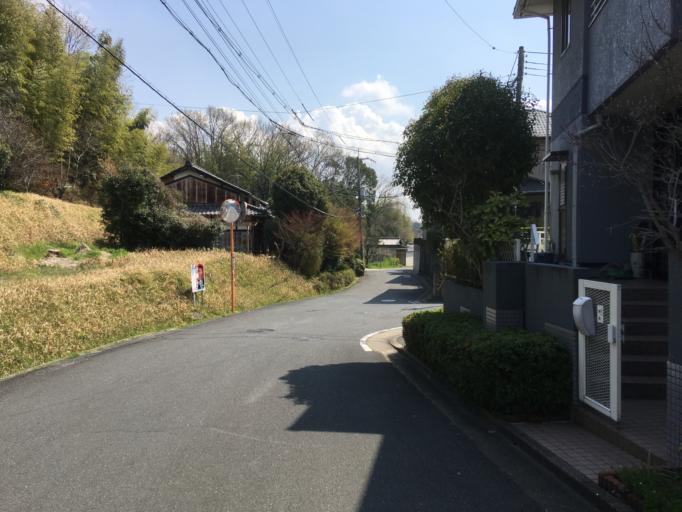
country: JP
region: Nara
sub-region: Ikoma-shi
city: Ikoma
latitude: 34.7432
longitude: 135.7170
